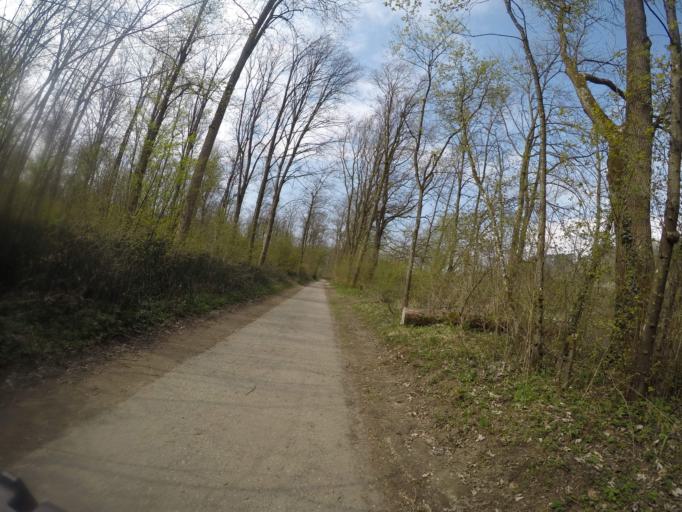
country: DE
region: Baden-Wuerttemberg
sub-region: Tuebingen Region
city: Ulm
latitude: 48.3817
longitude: 9.9748
